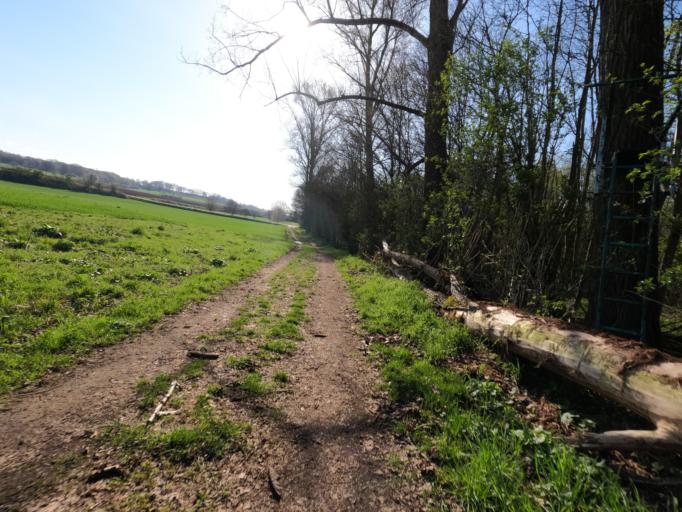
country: DE
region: North Rhine-Westphalia
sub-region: Regierungsbezirk Koln
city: Linnich
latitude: 50.9903
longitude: 6.2844
